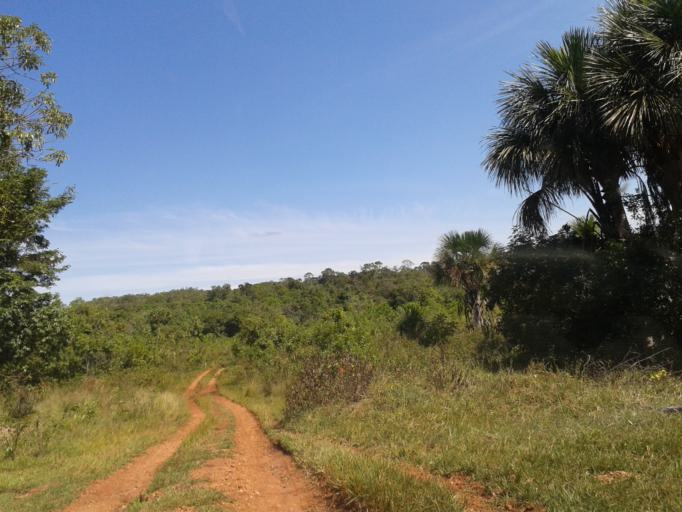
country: BR
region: Minas Gerais
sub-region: Campina Verde
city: Campina Verde
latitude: -19.4381
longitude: -49.6929
